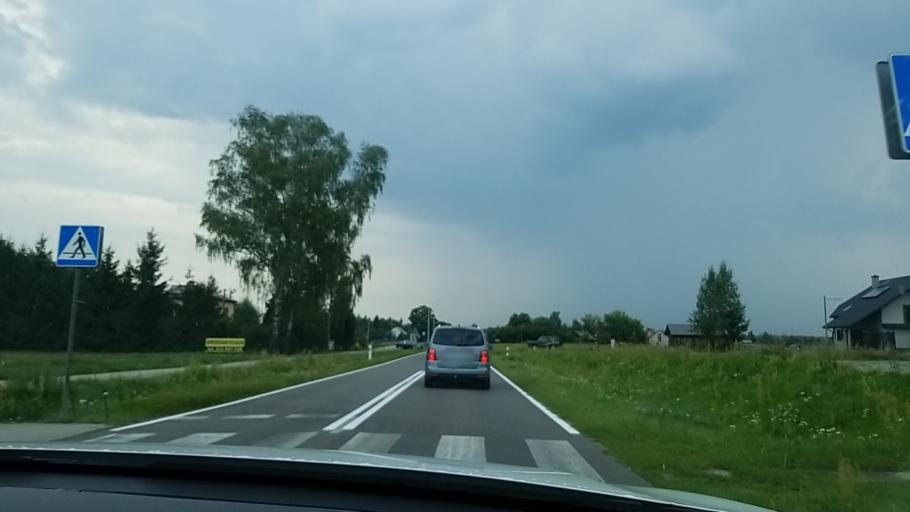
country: PL
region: Lublin Voivodeship
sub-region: Powiat wlodawski
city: Wlodawa
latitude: 51.5637
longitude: 23.5504
